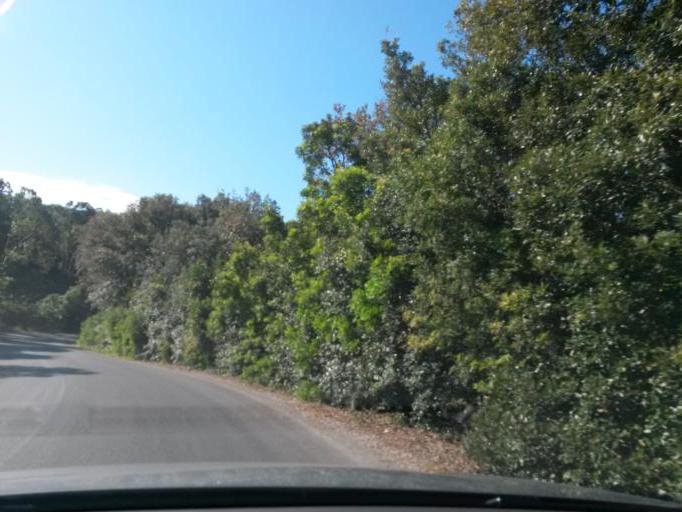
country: IT
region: Tuscany
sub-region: Provincia di Livorno
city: Campo nell'Elba
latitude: 42.7875
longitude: 10.2382
